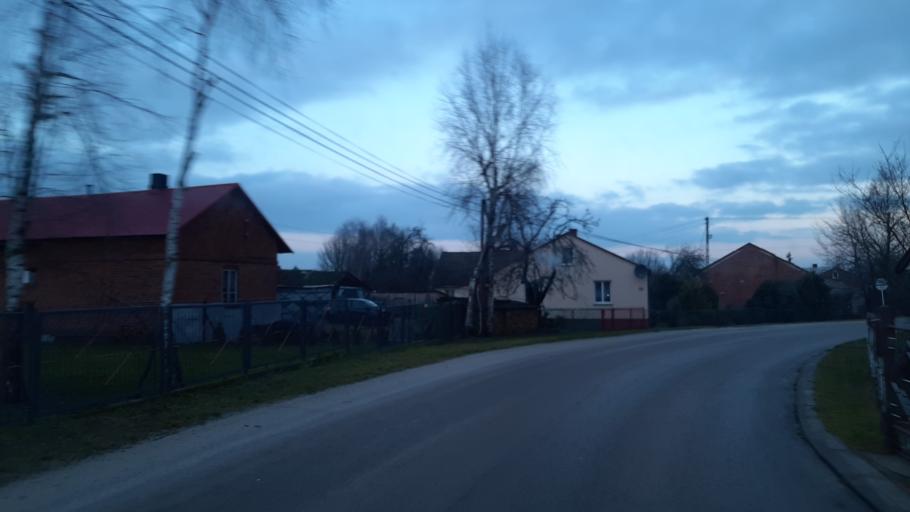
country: PL
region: Lublin Voivodeship
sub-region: Powiat lubartowski
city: Firlej
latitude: 51.5703
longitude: 22.5346
